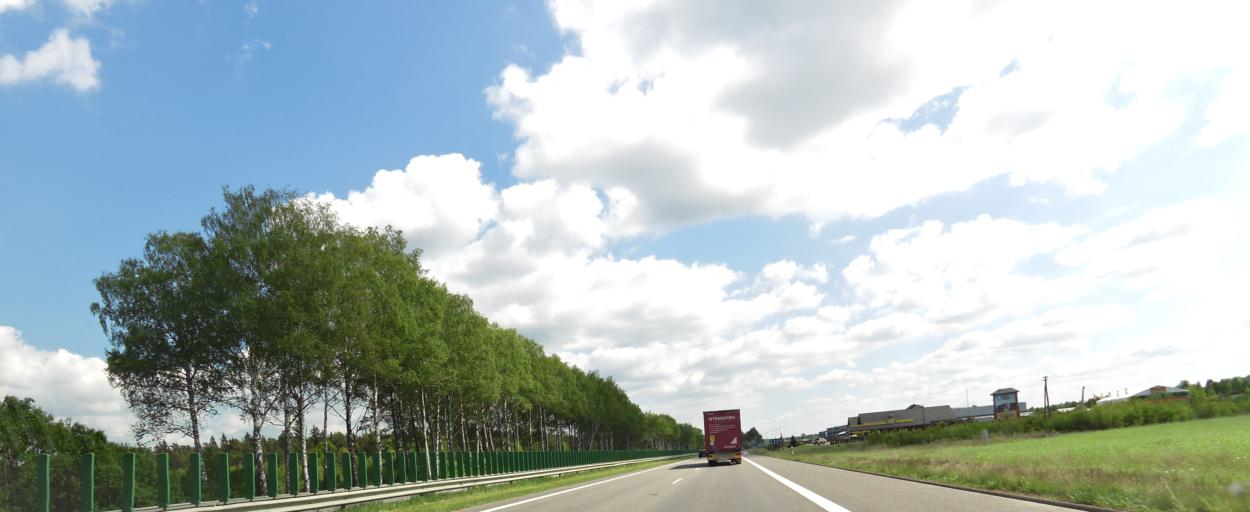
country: LT
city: Lentvaris
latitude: 54.7048
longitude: 25.0038
